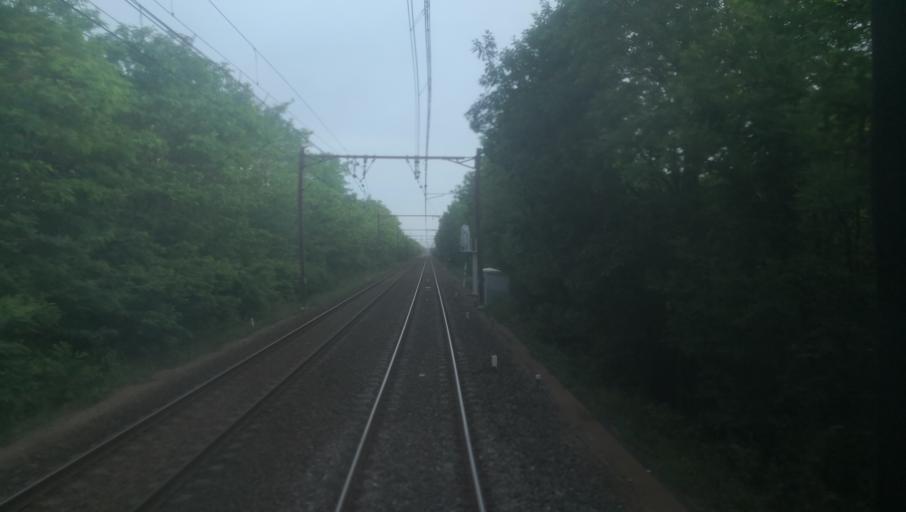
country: FR
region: Centre
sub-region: Departement du Loiret
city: Menestreau-en-Villette
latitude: 47.6584
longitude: 1.9749
